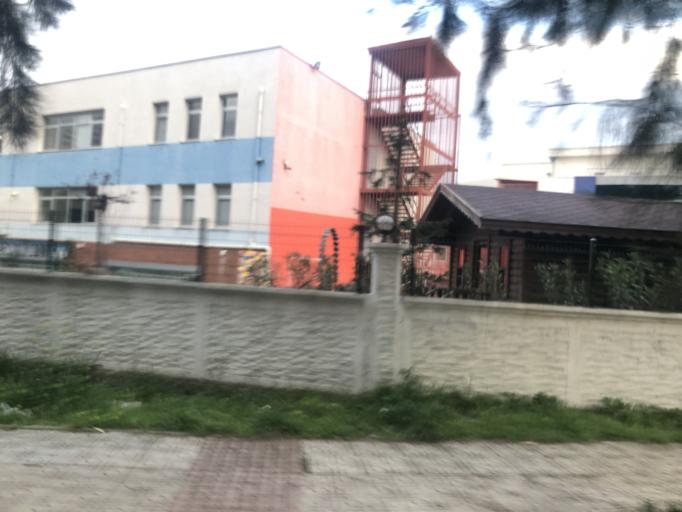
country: TR
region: Izmir
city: Karsiyaka
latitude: 38.4719
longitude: 27.0683
